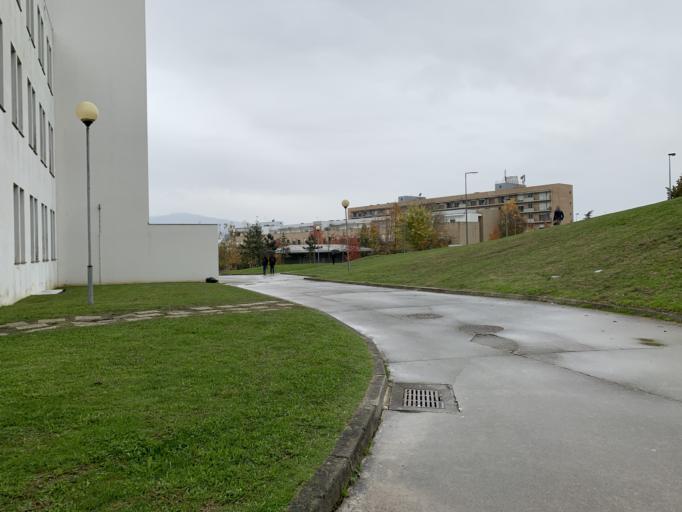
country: PT
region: Braga
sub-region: Braga
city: Braga
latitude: 41.5602
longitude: -8.3981
